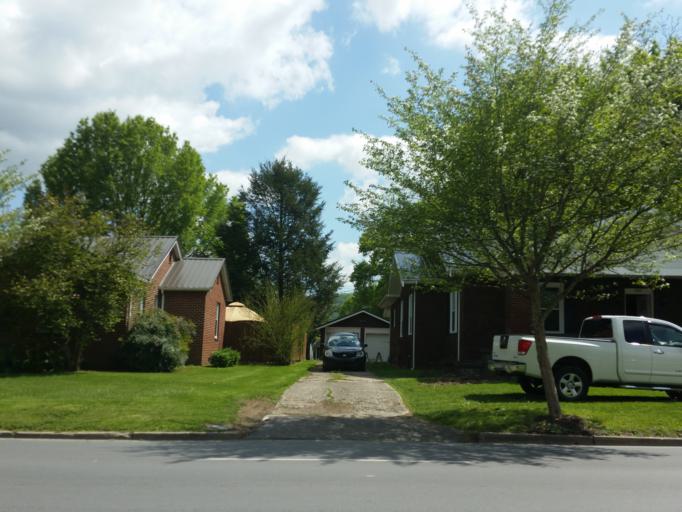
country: US
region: Kentucky
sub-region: Bell County
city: Middlesboro
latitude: 36.6061
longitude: -83.7287
